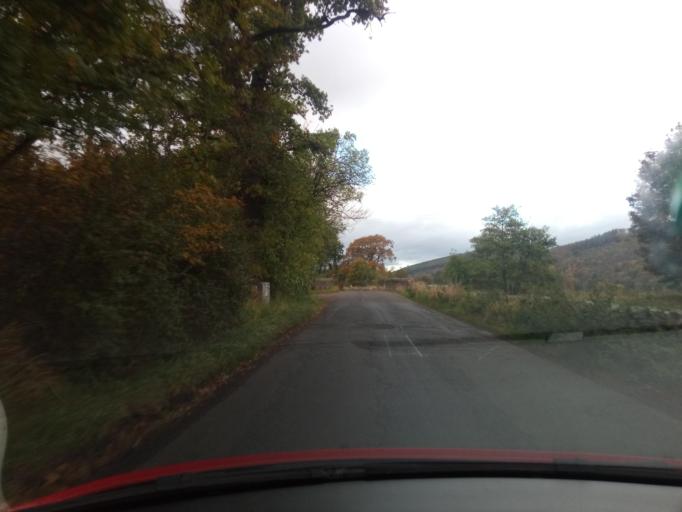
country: GB
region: Scotland
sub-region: The Scottish Borders
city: Peebles
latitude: 55.6417
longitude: -3.1608
